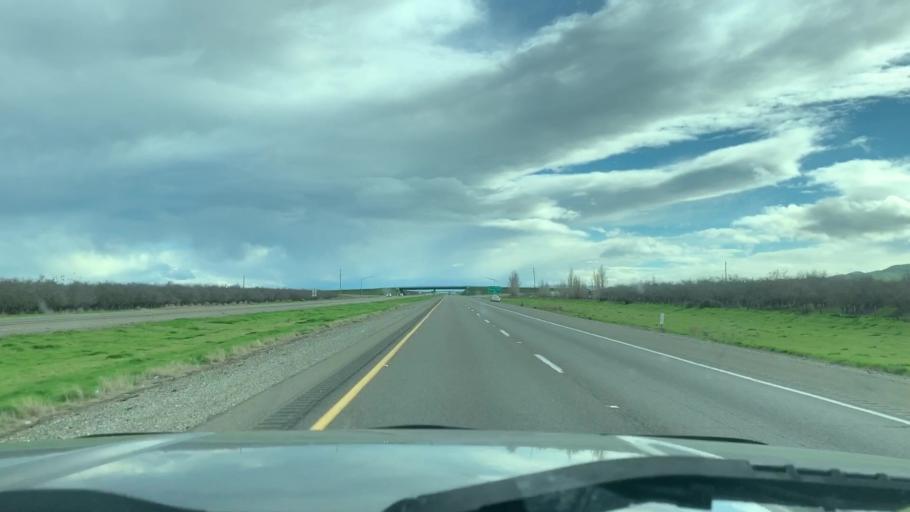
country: US
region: California
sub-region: Merced County
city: South Dos Palos
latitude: 36.7839
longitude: -120.7286
